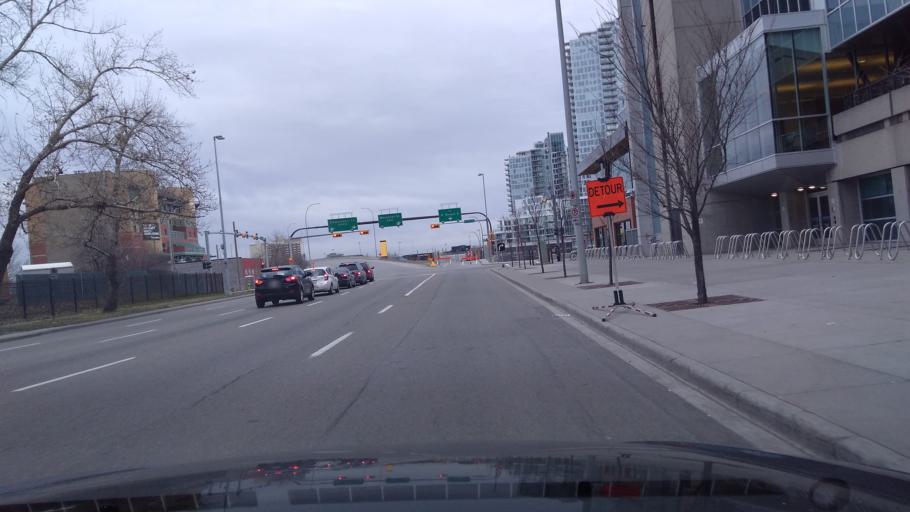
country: CA
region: Alberta
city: Calgary
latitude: 51.0481
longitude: -114.0566
